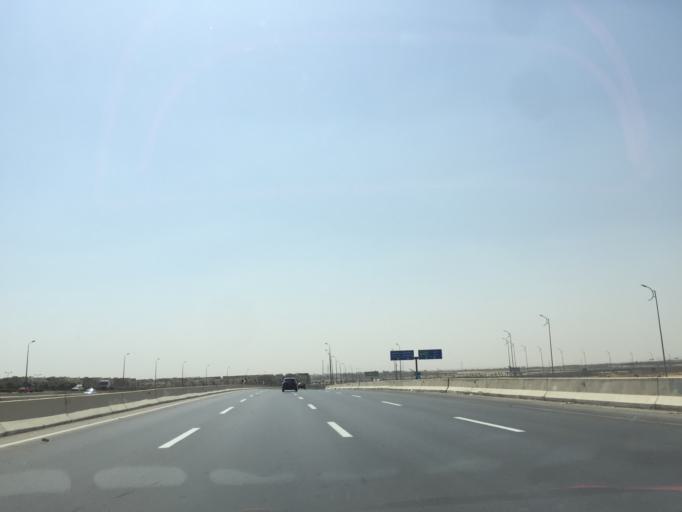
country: EG
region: Al Jizah
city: Awsim
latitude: 30.0754
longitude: 30.9459
